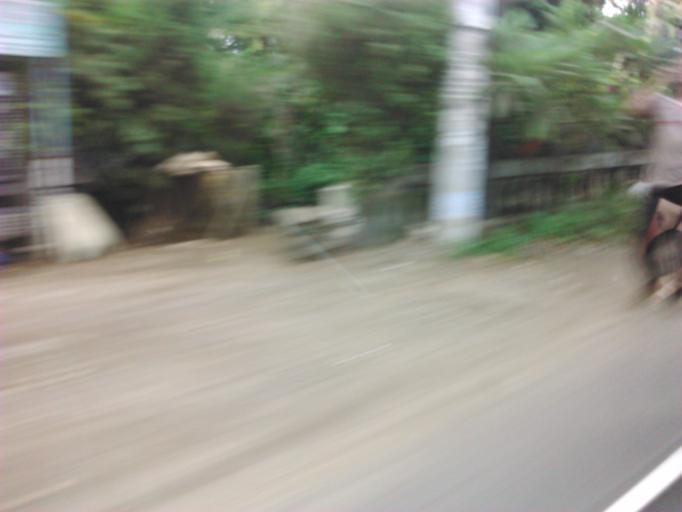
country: ID
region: East Java
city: Wonorejo
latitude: -7.2905
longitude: 112.7944
